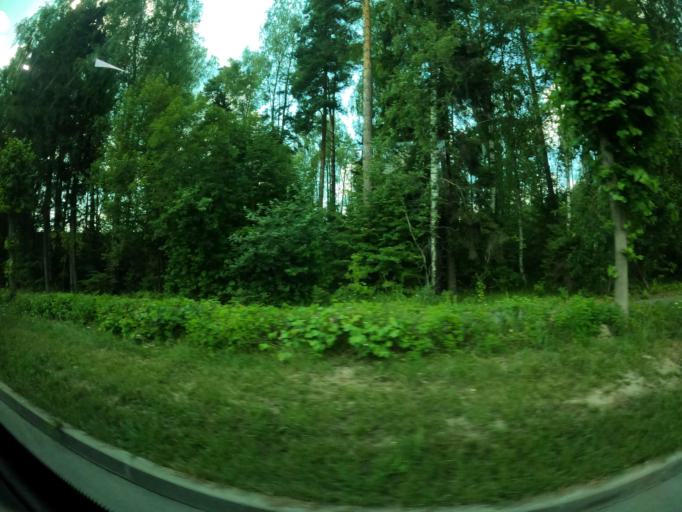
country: RU
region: Moskovskaya
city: Protvino
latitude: 54.8751
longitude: 37.2297
